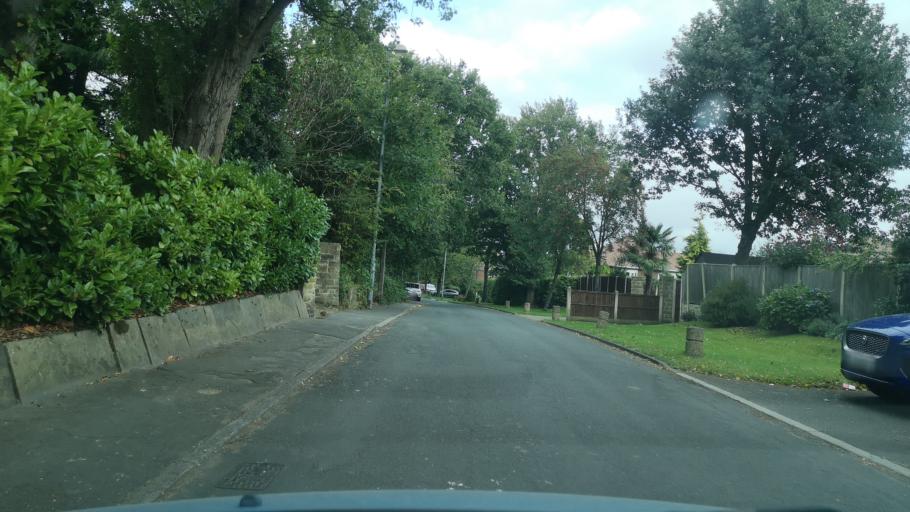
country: GB
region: England
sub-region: City and Borough of Wakefield
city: Walton
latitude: 53.6575
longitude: -1.4885
